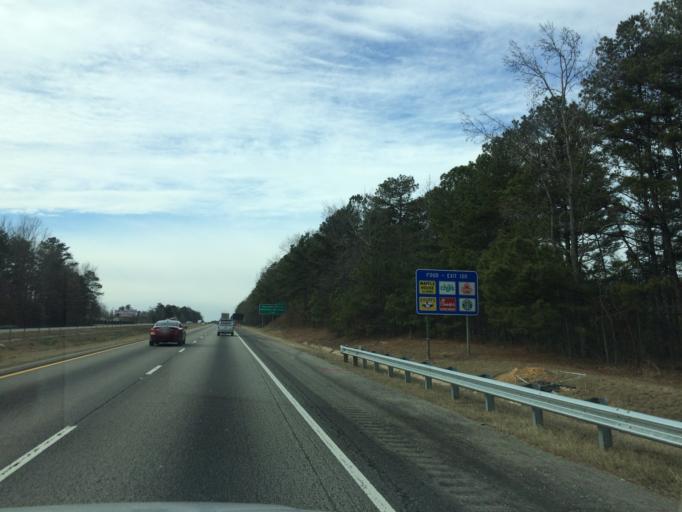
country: US
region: Georgia
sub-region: Gwinnett County
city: Dacula
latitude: 34.0769
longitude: -83.8958
